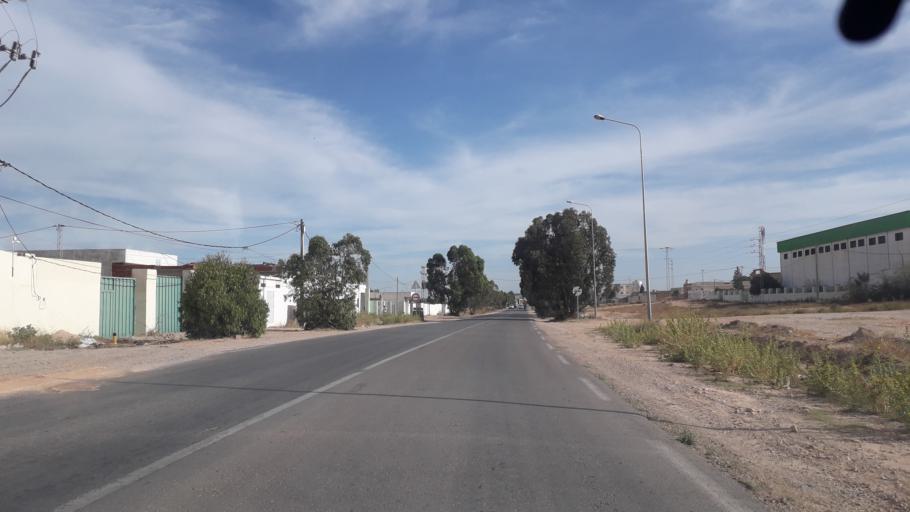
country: TN
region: Safaqis
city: Al Qarmadah
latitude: 34.8905
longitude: 10.7629
